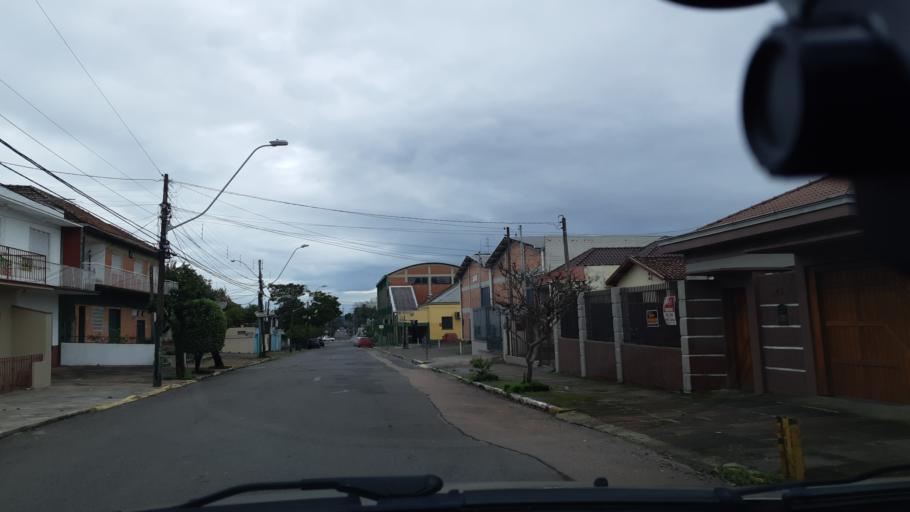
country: BR
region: Rio Grande do Sul
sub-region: Sao Leopoldo
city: Sao Leopoldo
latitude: -29.7761
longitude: -51.1526
